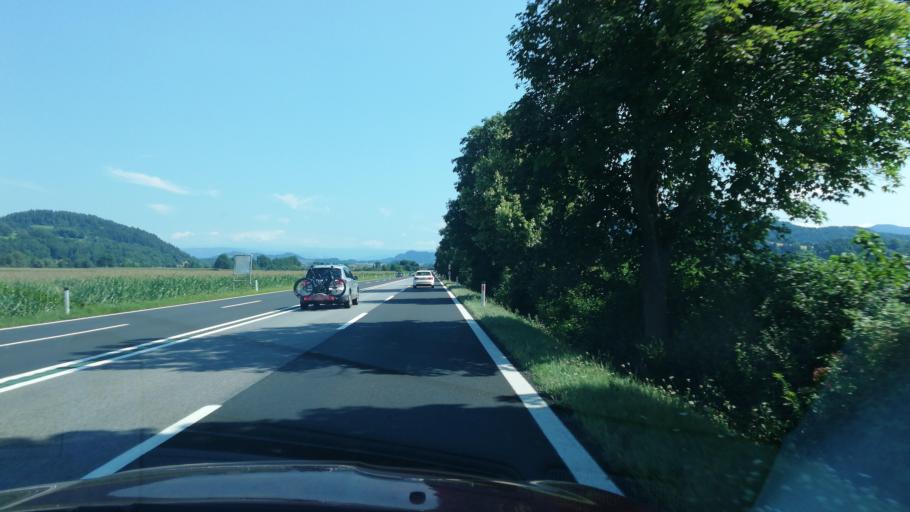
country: AT
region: Carinthia
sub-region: Politischer Bezirk Klagenfurt Land
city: Maria Saal
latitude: 46.6913
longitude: 14.3463
